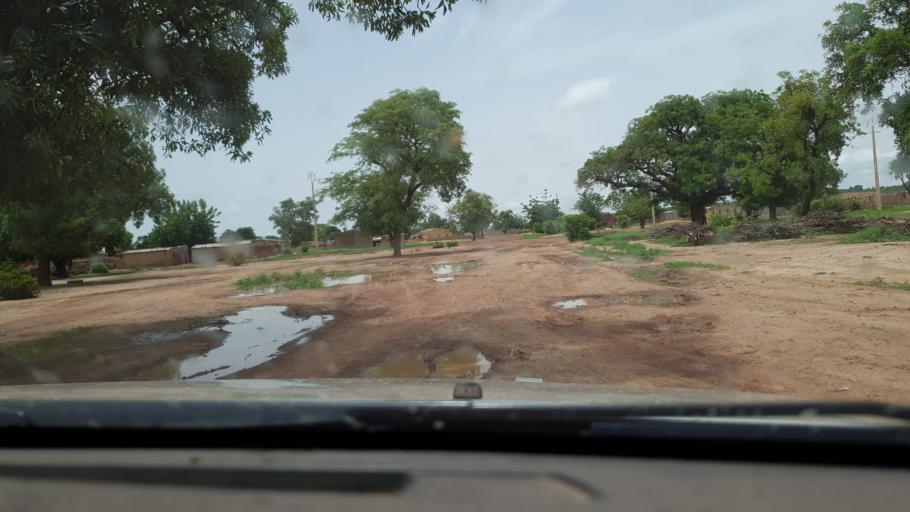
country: ML
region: Koulikoro
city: Dioila
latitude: 12.5217
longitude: -6.8110
